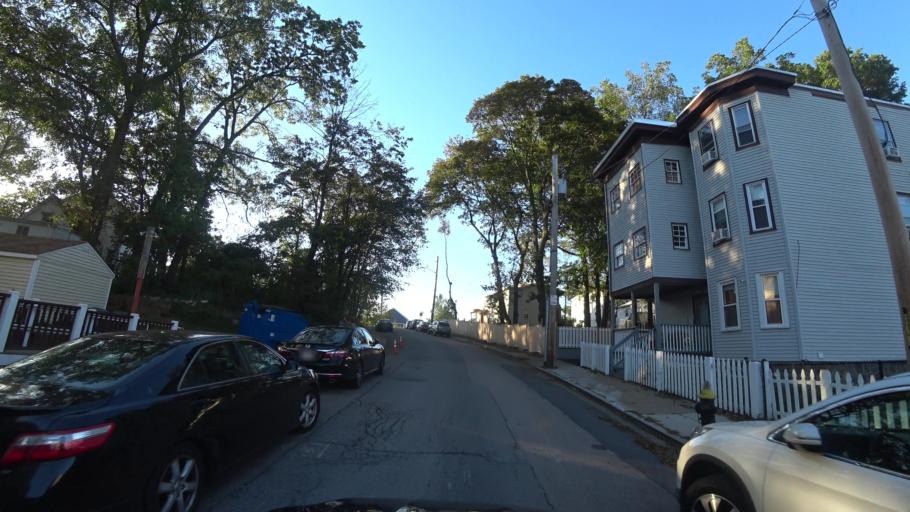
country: US
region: Massachusetts
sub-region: Suffolk County
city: Jamaica Plain
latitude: 42.2900
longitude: -71.0910
